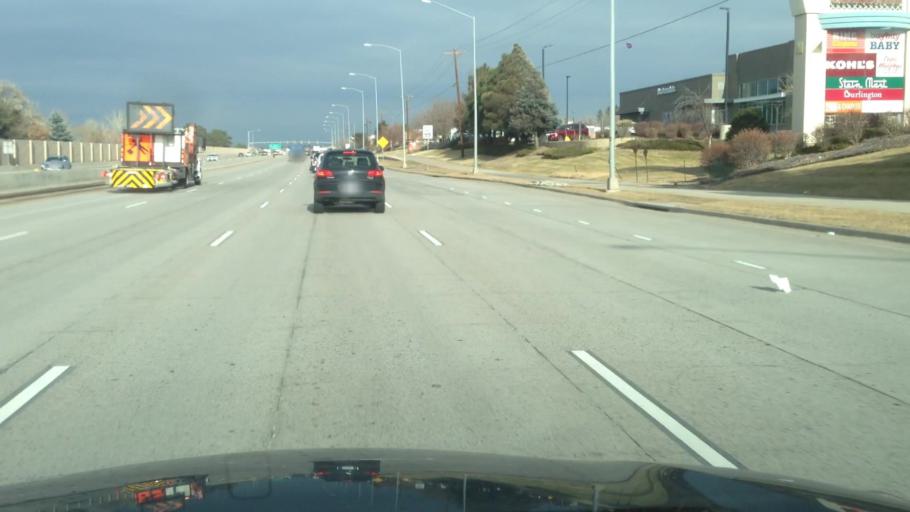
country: US
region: Colorado
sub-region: Arapahoe County
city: Dove Valley
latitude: 39.5983
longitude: -104.8039
